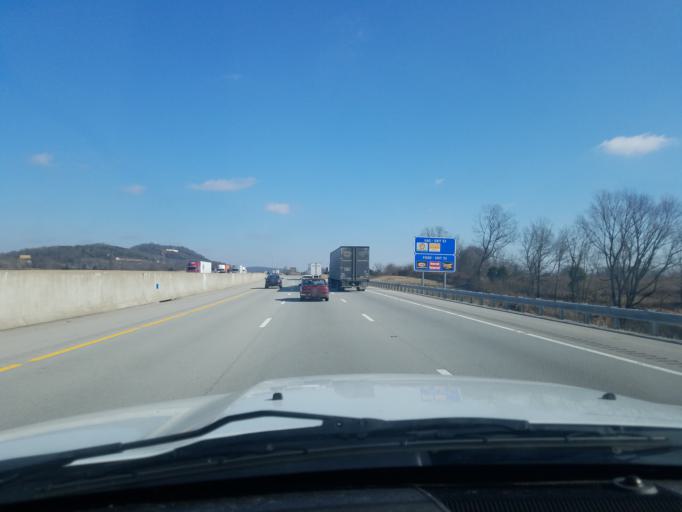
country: US
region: Kentucky
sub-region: Barren County
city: Cave City
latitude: 37.1264
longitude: -85.9888
